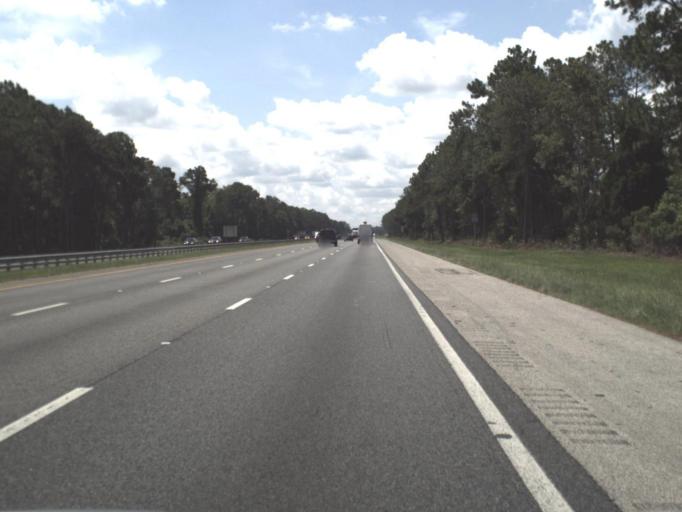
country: US
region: Florida
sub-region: Saint Johns County
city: Saint Augustine South
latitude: 29.8195
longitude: -81.3764
